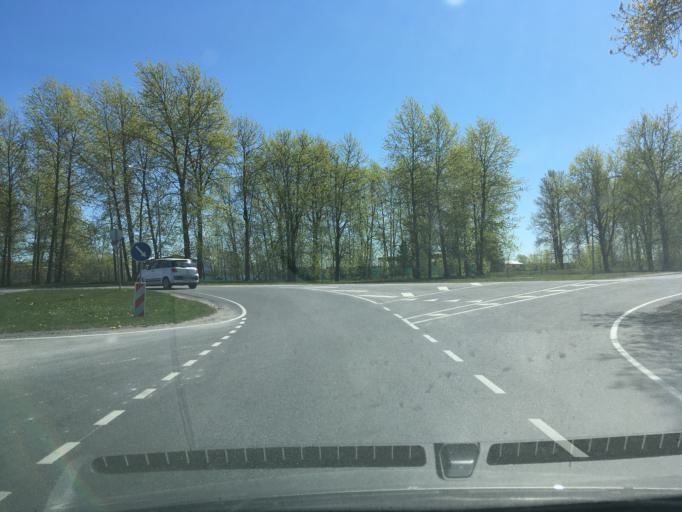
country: EE
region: Harju
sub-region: Maardu linn
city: Maardu
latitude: 59.4549
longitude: 24.9992
